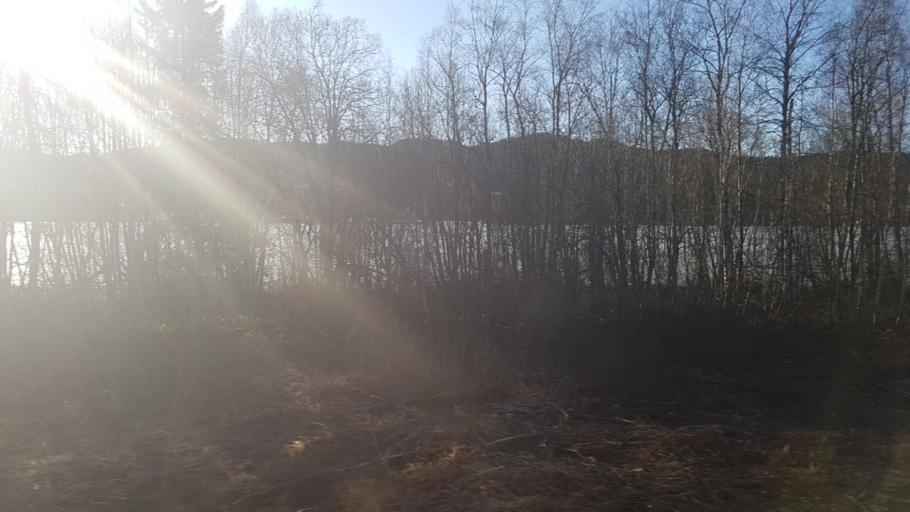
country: NO
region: Nord-Trondelag
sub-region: Levanger
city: Skogn
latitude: 63.6508
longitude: 11.0873
